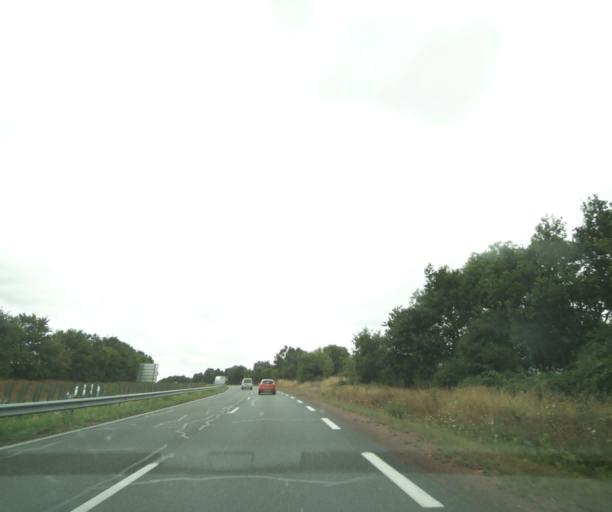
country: FR
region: Pays de la Loire
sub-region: Departement de la Vendee
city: Saint-Denis-la-Chevasse
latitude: 46.8684
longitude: -1.4012
